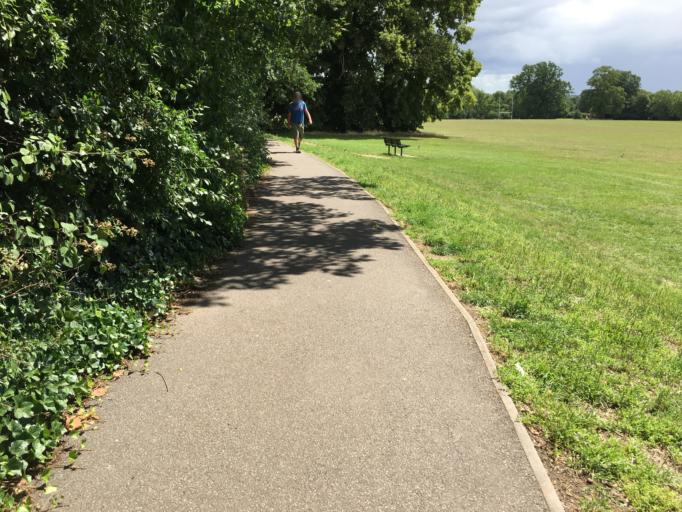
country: GB
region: England
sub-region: West Berkshire
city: Tilehurst
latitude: 51.4481
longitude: -1.0143
